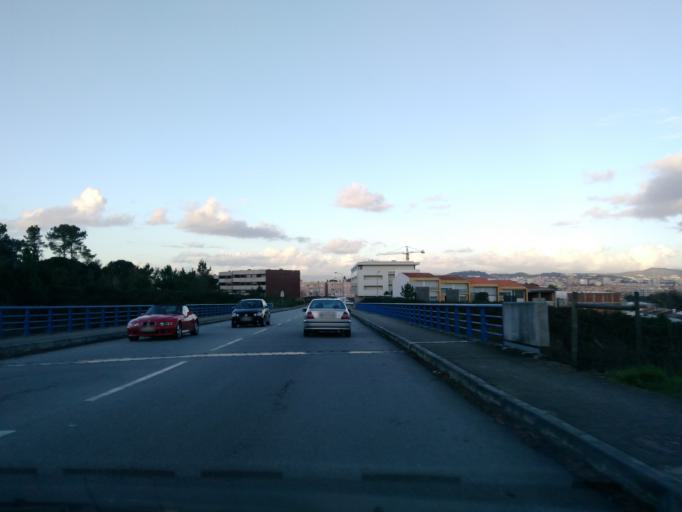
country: PT
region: Braga
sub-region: Braga
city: Braga
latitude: 41.5315
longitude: -8.4543
